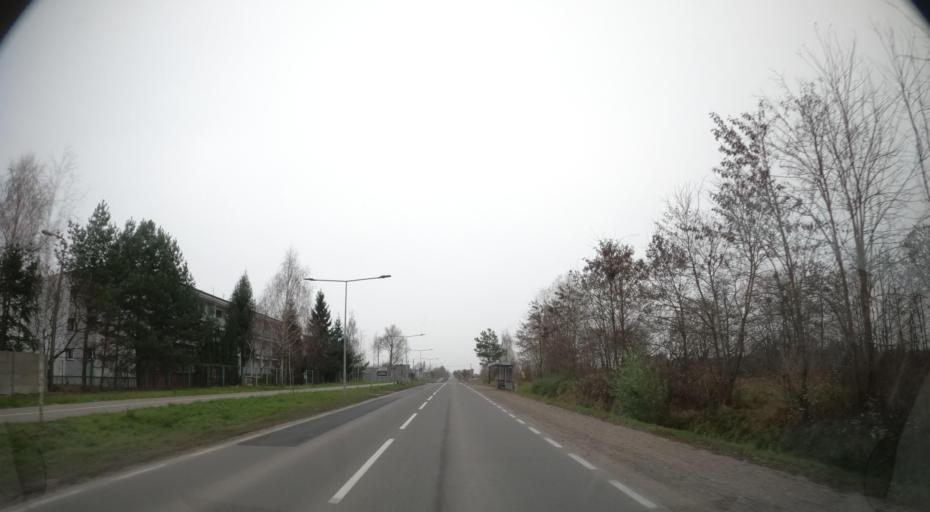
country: PL
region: Masovian Voivodeship
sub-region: Radom
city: Radom
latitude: 51.4454
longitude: 21.1915
